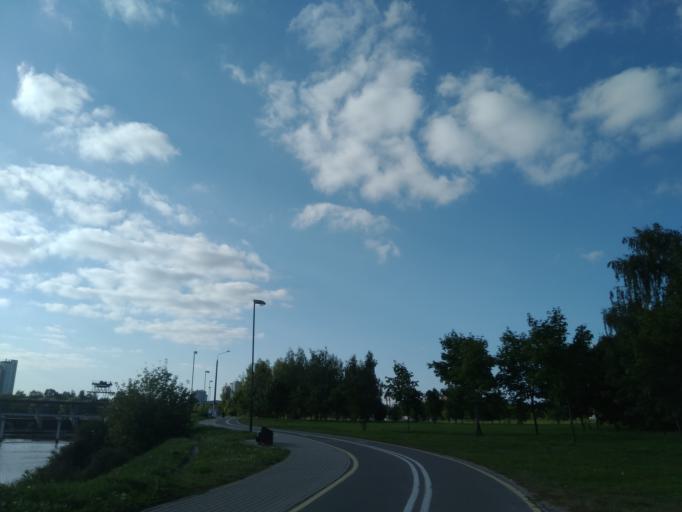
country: BY
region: Minsk
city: Minsk
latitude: 53.8756
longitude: 27.5839
